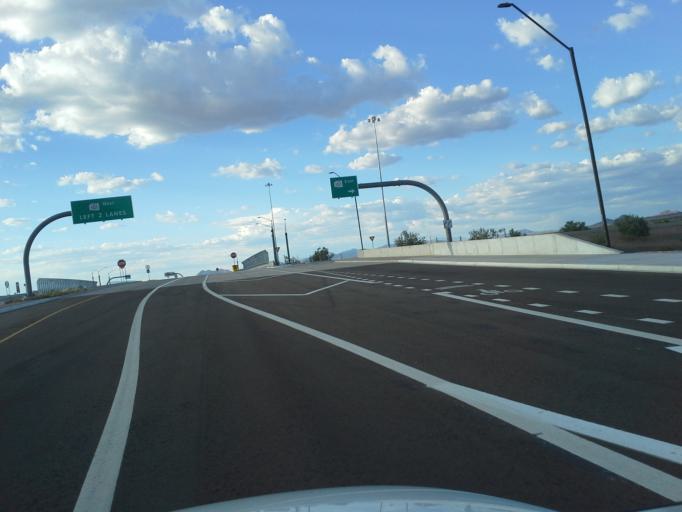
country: US
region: Arizona
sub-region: Maricopa County
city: Paradise Valley
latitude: 33.6600
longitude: -111.9426
